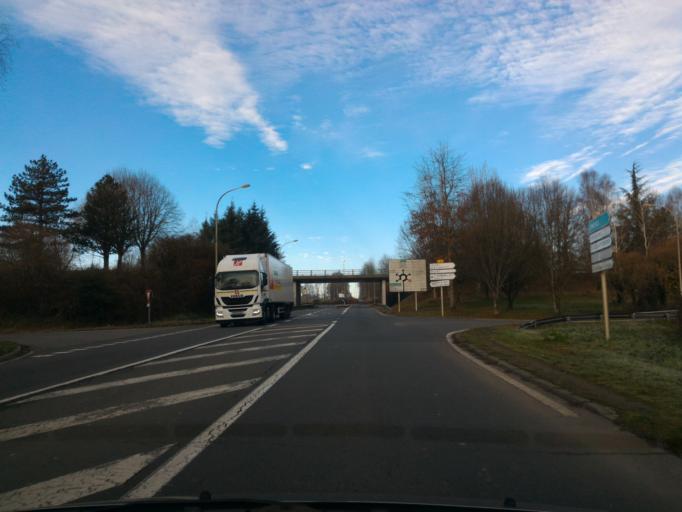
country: FR
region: Poitou-Charentes
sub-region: Departement de la Charente
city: Confolens
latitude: 46.0229
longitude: 0.6548
